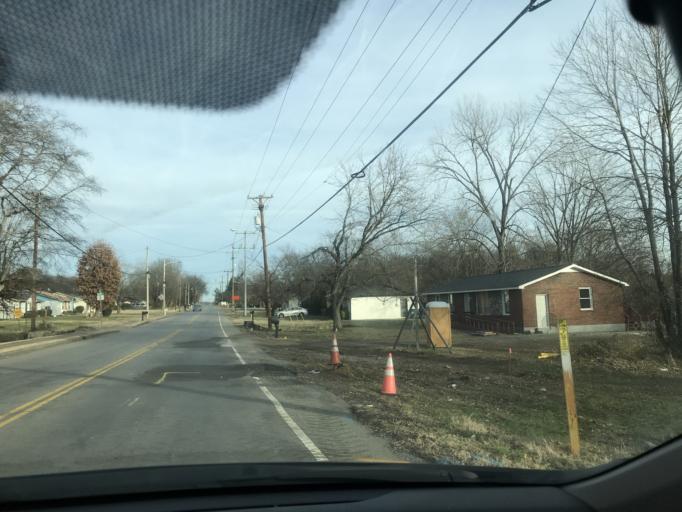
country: US
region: Tennessee
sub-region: Davidson County
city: Nashville
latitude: 36.2186
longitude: -86.8360
